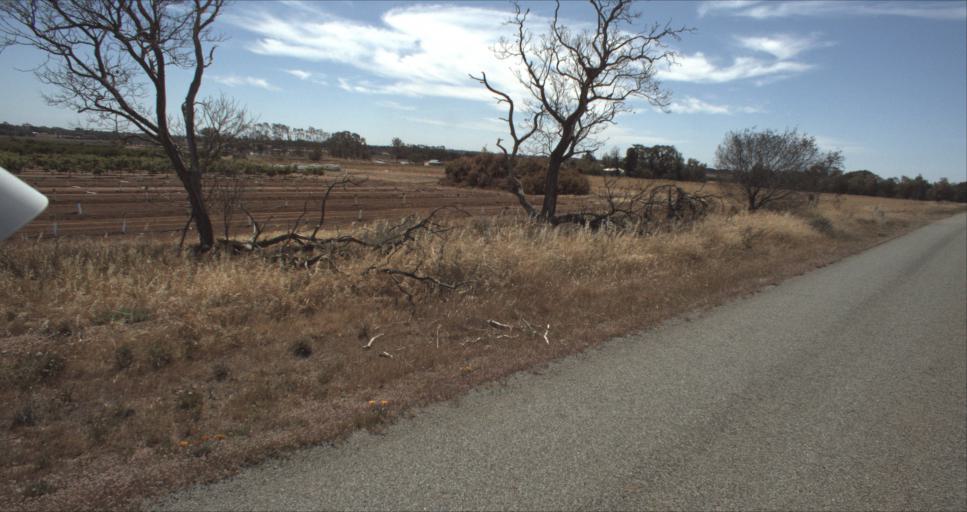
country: AU
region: New South Wales
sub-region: Leeton
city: Leeton
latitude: -34.6106
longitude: 146.4346
